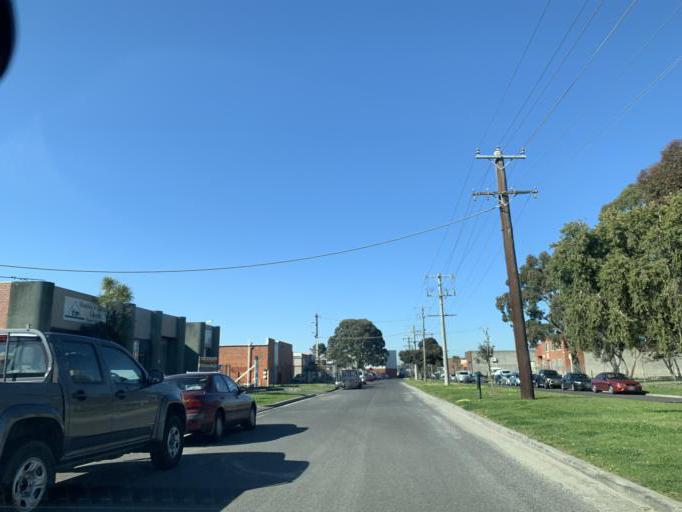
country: AU
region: Victoria
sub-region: Greater Dandenong
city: Dandenong
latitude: -37.9875
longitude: 145.1972
